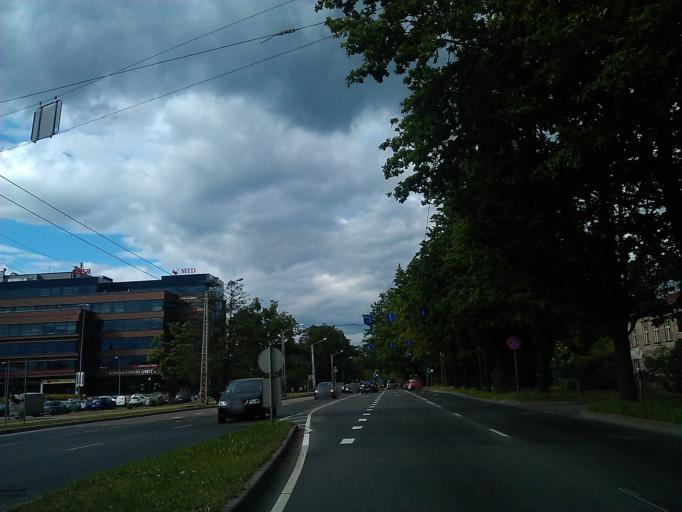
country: LV
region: Marupe
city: Marupe
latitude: 56.9070
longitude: 24.0837
